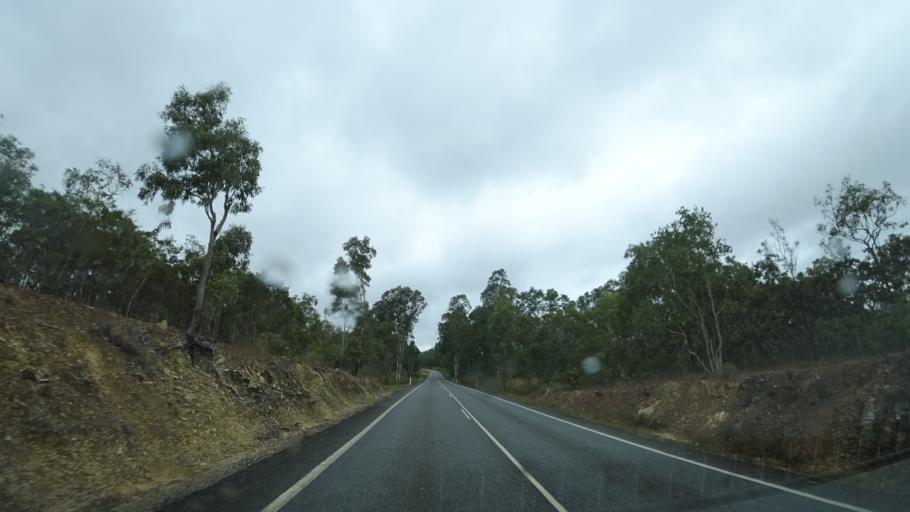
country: AU
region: Queensland
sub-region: Cairns
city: Port Douglas
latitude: -16.6895
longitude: 145.3354
